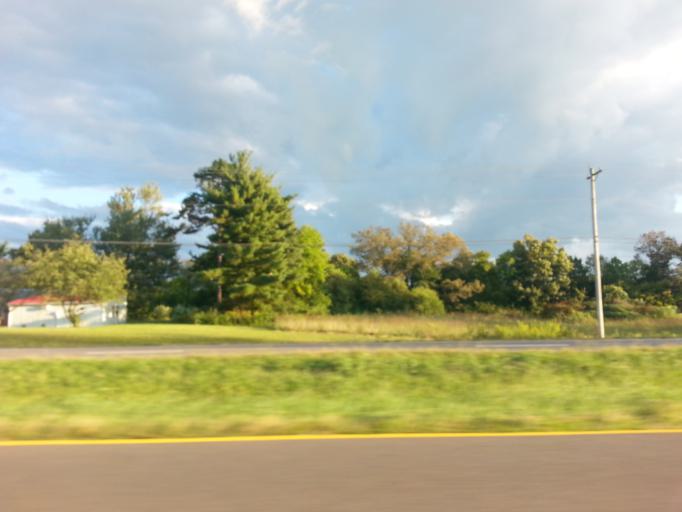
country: US
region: Tennessee
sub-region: Jefferson County
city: New Market
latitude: 36.1065
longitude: -83.5300
